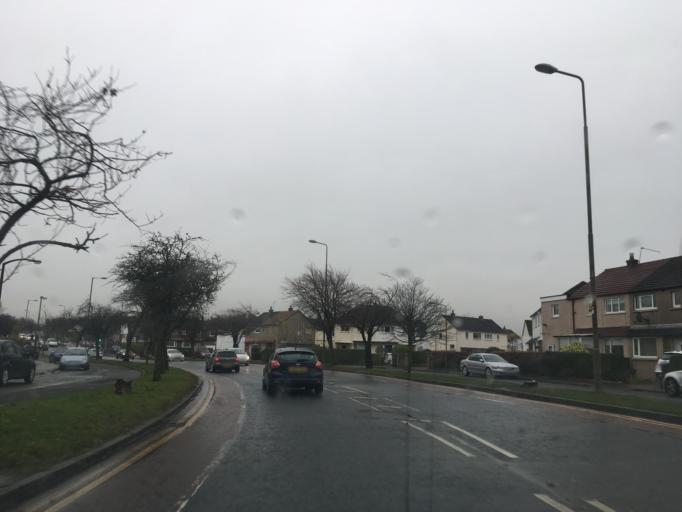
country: GB
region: Scotland
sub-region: Edinburgh
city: Currie
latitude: 55.9393
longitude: -3.2930
